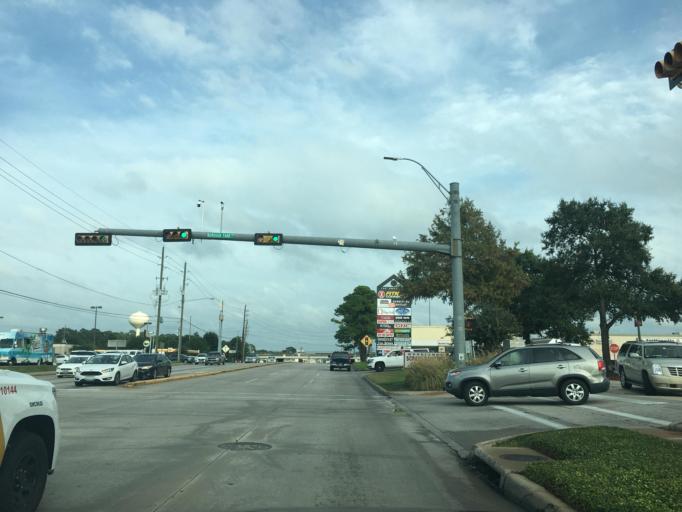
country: US
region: Texas
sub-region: Montgomery County
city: Oak Ridge North
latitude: 30.1266
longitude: -95.4465
